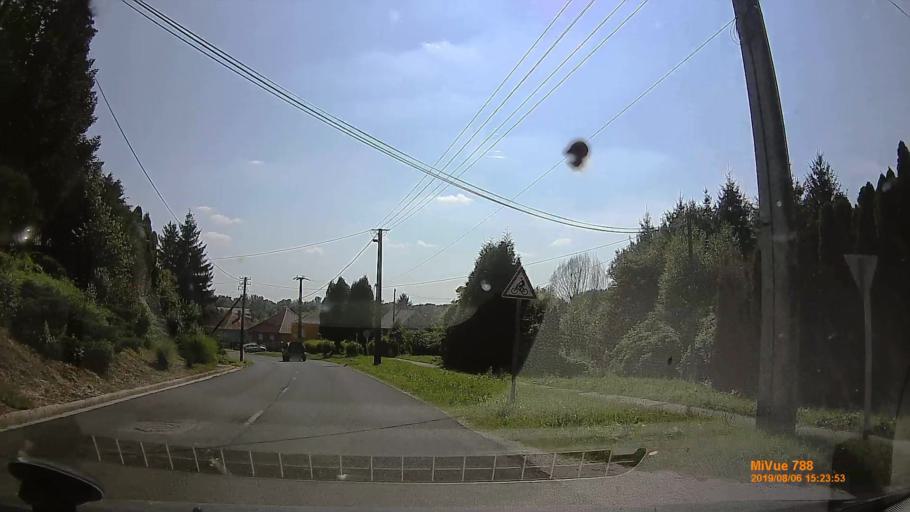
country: HR
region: Koprivnicko-Krizevacka
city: Drnje
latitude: 46.2584
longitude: 16.9413
